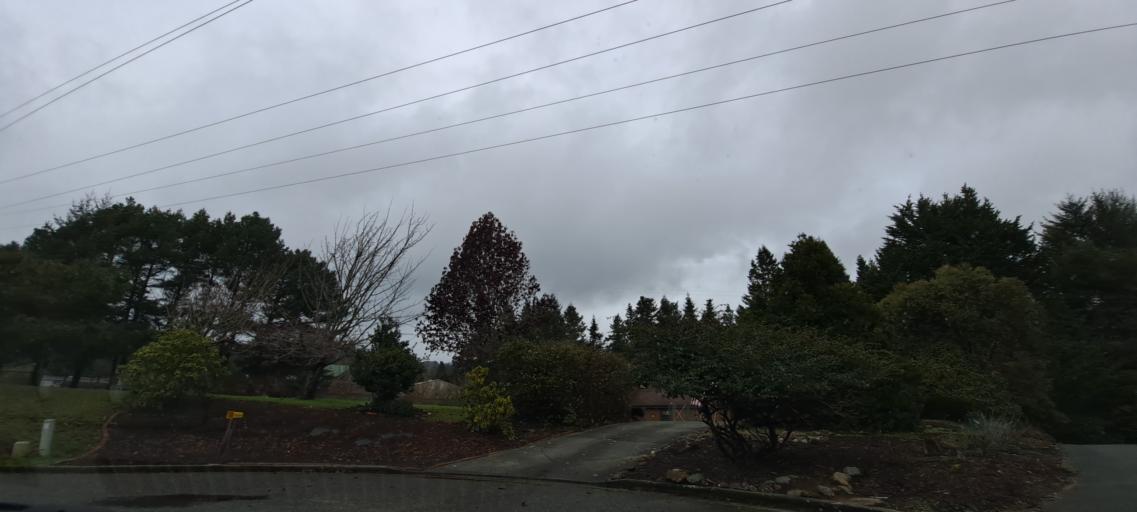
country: US
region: California
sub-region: Humboldt County
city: Fortuna
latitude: 40.6014
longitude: -124.1391
